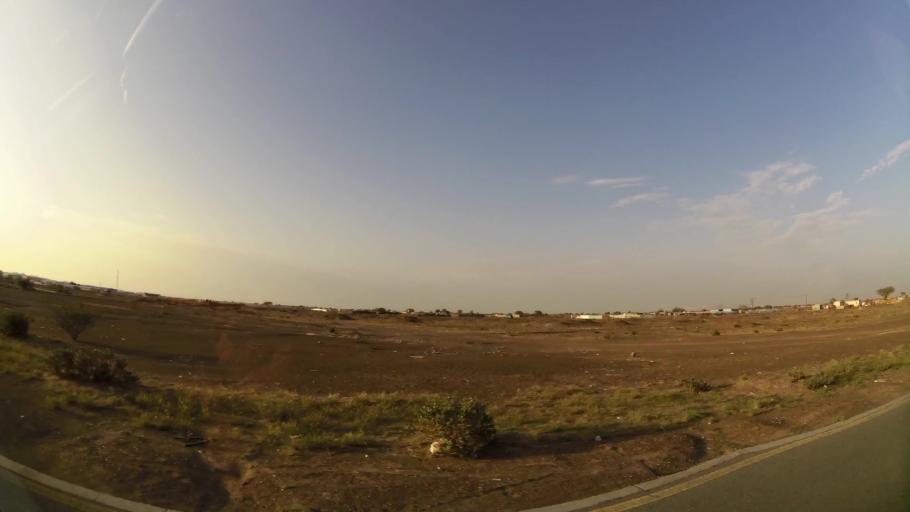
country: AE
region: Abu Dhabi
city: Al Ain
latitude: 24.1553
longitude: 55.8300
